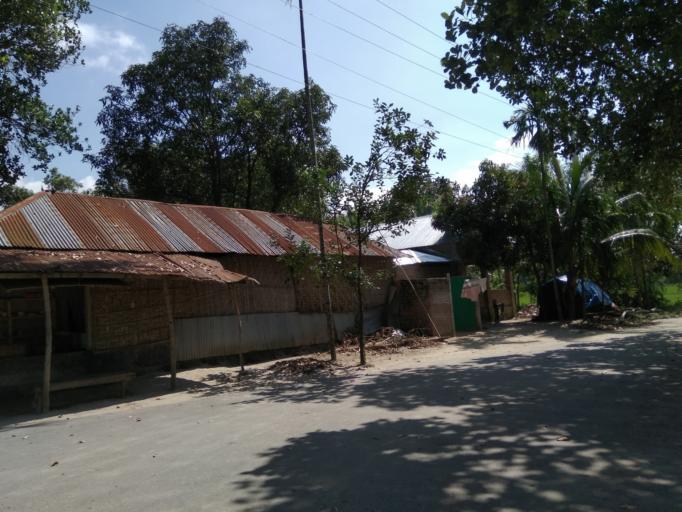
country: IN
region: West Bengal
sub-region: Koch Bihar
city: Haldibari
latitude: 26.1923
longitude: 88.6911
